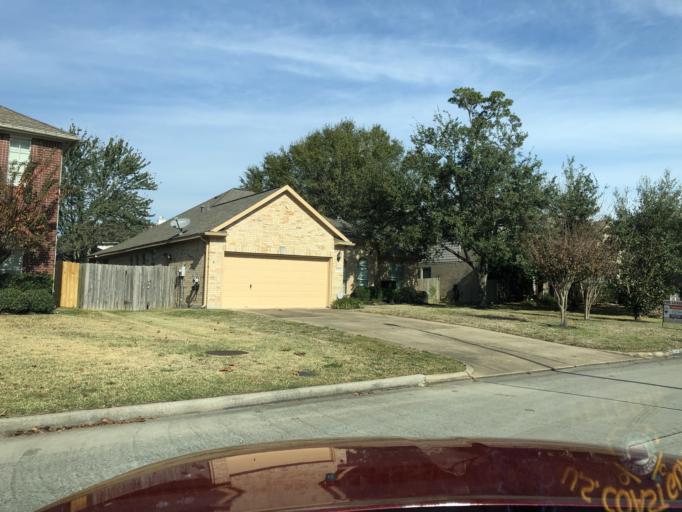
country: US
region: Texas
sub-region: Harris County
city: Tomball
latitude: 30.0261
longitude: -95.5582
